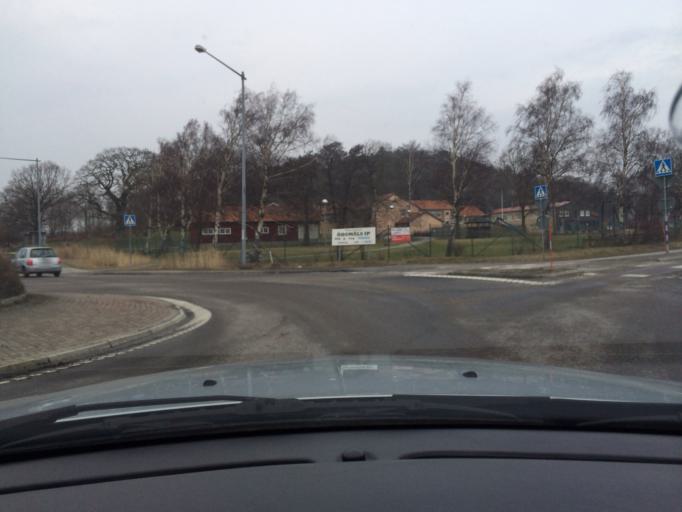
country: SE
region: Vaestra Goetaland
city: Svanesund
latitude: 58.1064
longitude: 11.8513
